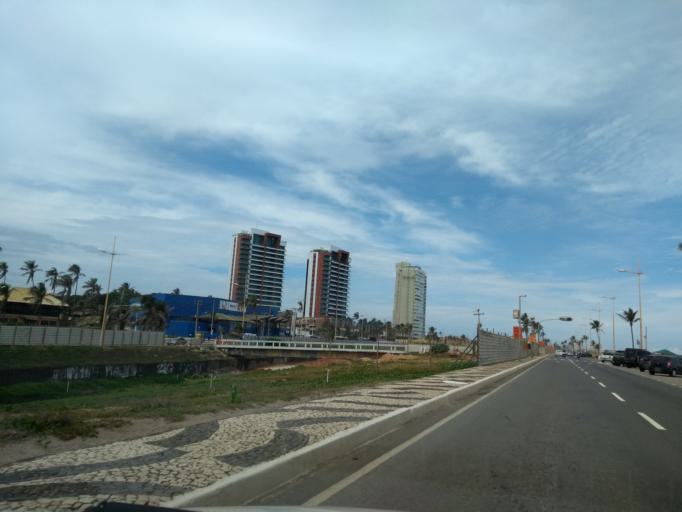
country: BR
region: Bahia
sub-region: Lauro De Freitas
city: Lauro de Freitas
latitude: -12.9611
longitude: -38.3970
